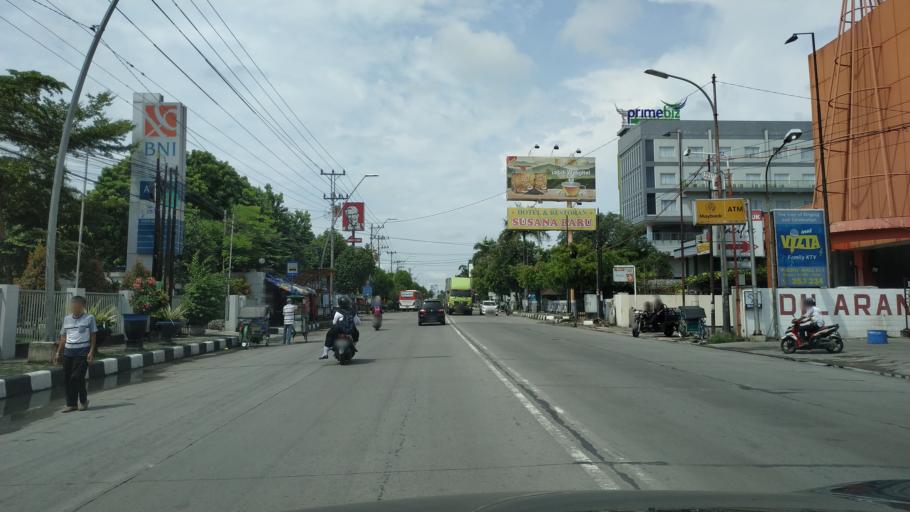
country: ID
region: Central Java
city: Tegal
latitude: -6.8694
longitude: 109.1293
